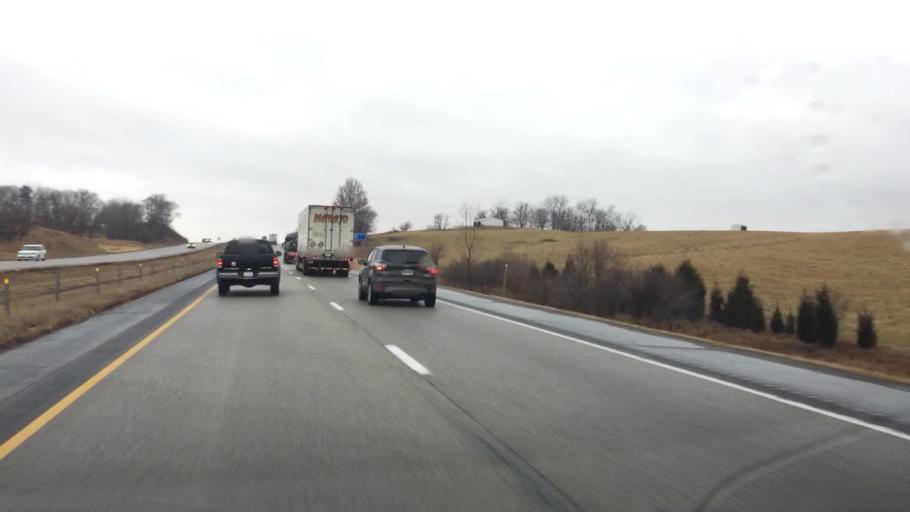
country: US
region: Iowa
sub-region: Johnson County
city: Tiffin
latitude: 41.6952
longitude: -91.7116
